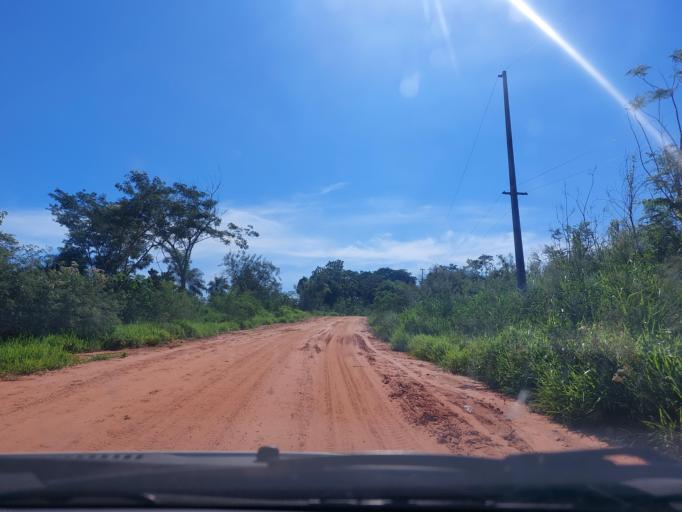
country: PY
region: San Pedro
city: Itacurubi del Rosario
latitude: -24.5423
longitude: -56.5838
